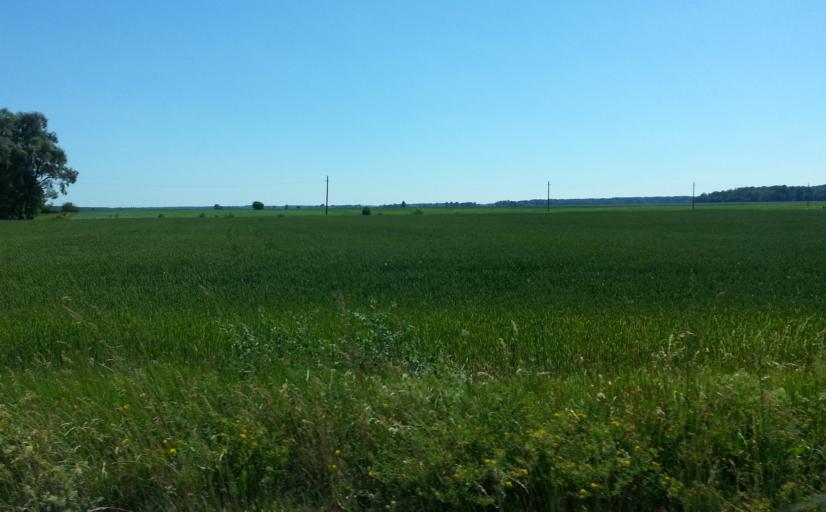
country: LT
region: Panevezys
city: Pasvalys
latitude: 56.2248
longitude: 24.4947
